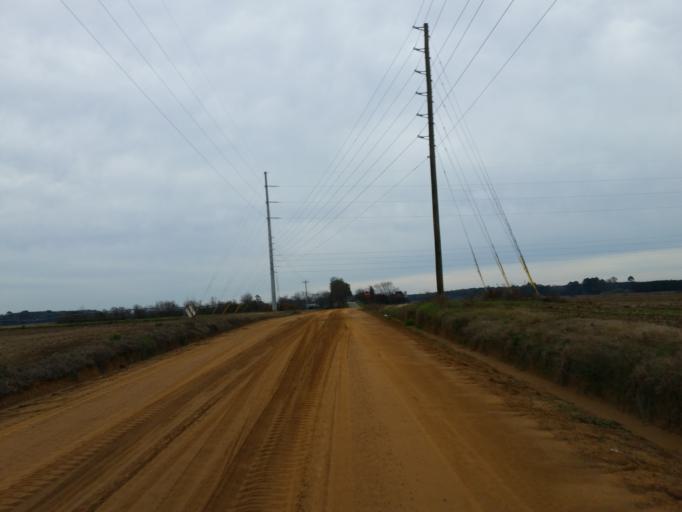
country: US
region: Georgia
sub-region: Dooly County
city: Vienna
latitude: 32.1442
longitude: -83.7623
